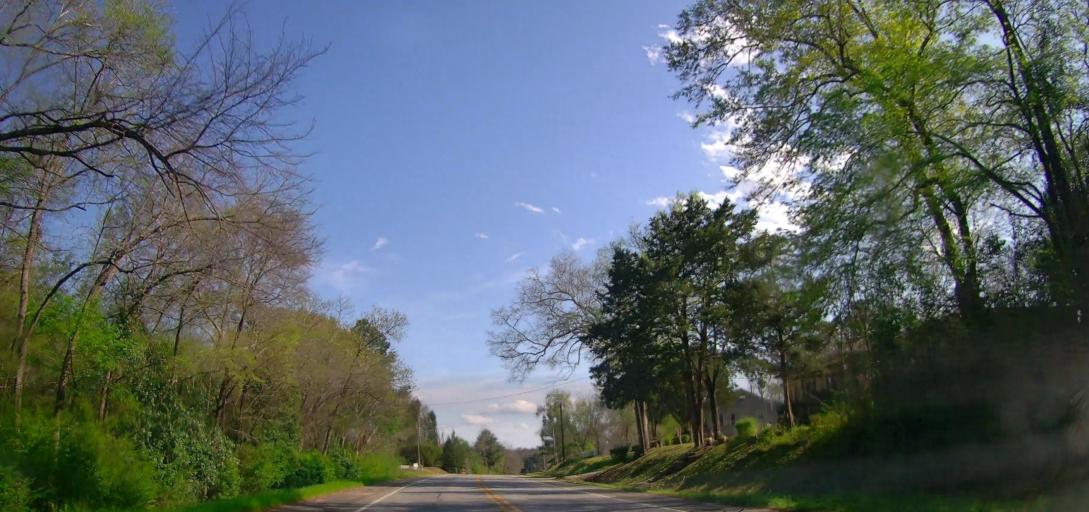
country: US
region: Georgia
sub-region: Baldwin County
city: Milledgeville
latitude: 33.0865
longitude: -83.2462
